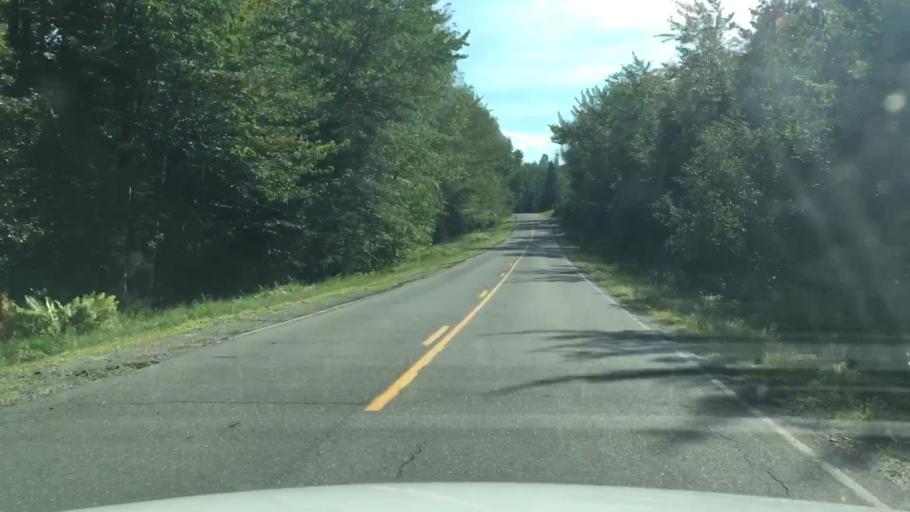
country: US
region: Maine
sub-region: Penobscot County
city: Enfield
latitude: 45.2953
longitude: -68.5549
